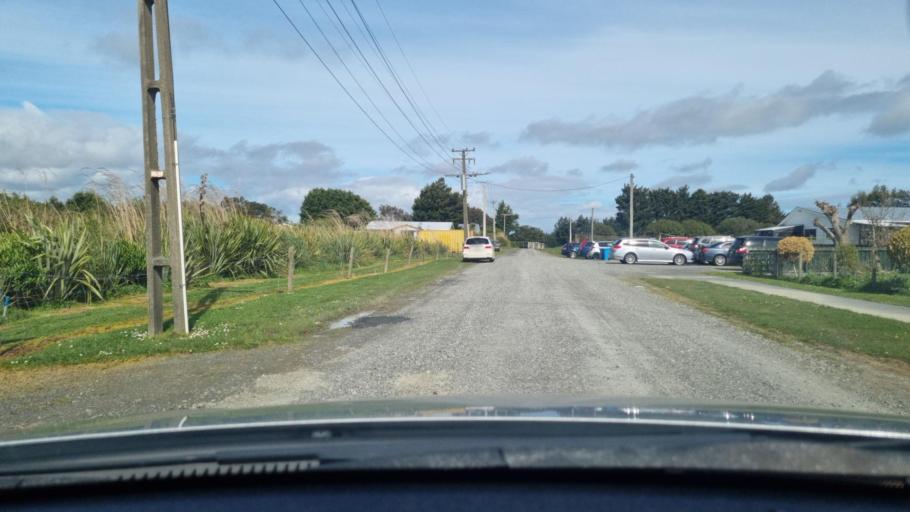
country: NZ
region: Southland
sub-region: Invercargill City
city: Invercargill
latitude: -46.4536
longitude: 168.3703
